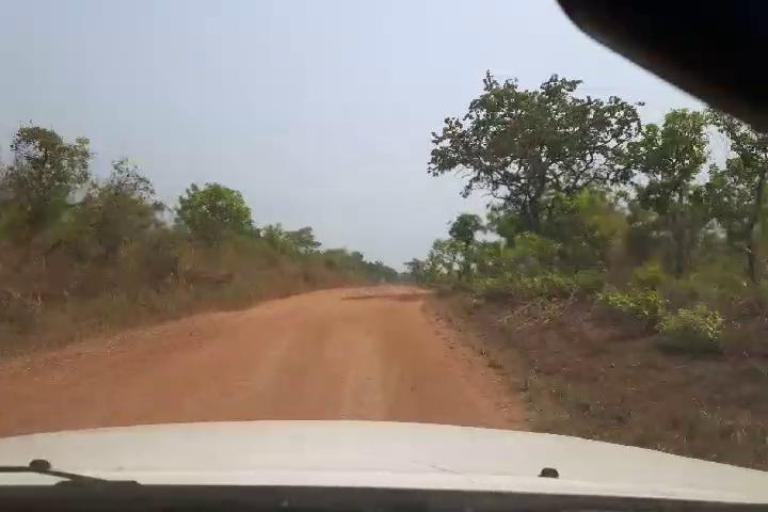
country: SL
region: Northern Province
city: Bumbuna
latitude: 8.9371
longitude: -11.8170
